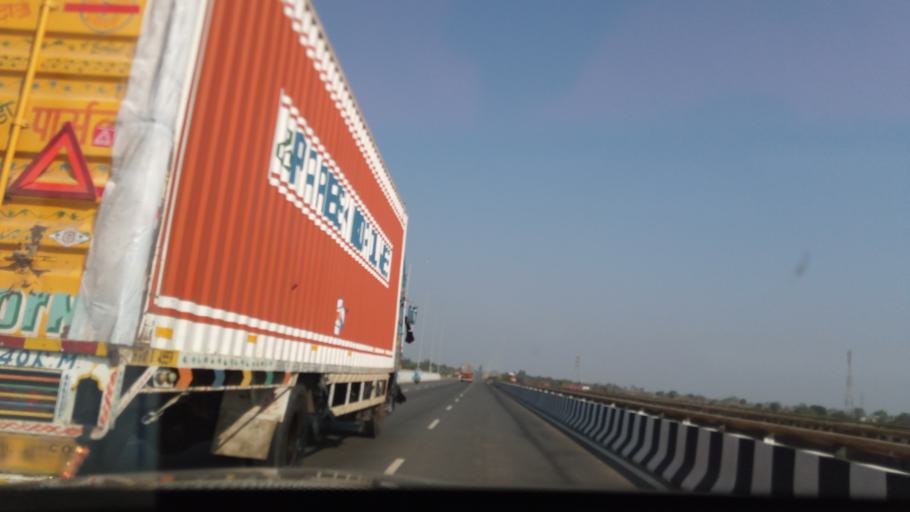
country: IN
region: Karnataka
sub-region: Haveri
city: Haveri
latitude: 14.8628
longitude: 75.3218
